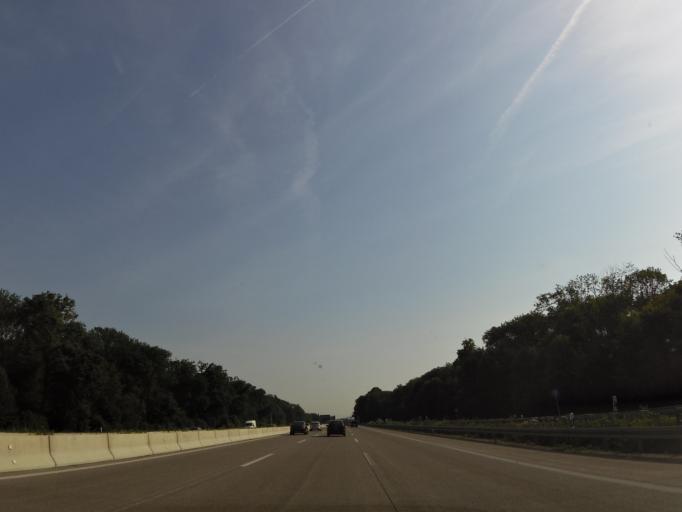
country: DE
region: Baden-Wuerttemberg
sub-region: Karlsruhe Region
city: Forst
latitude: 49.1492
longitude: 8.5609
